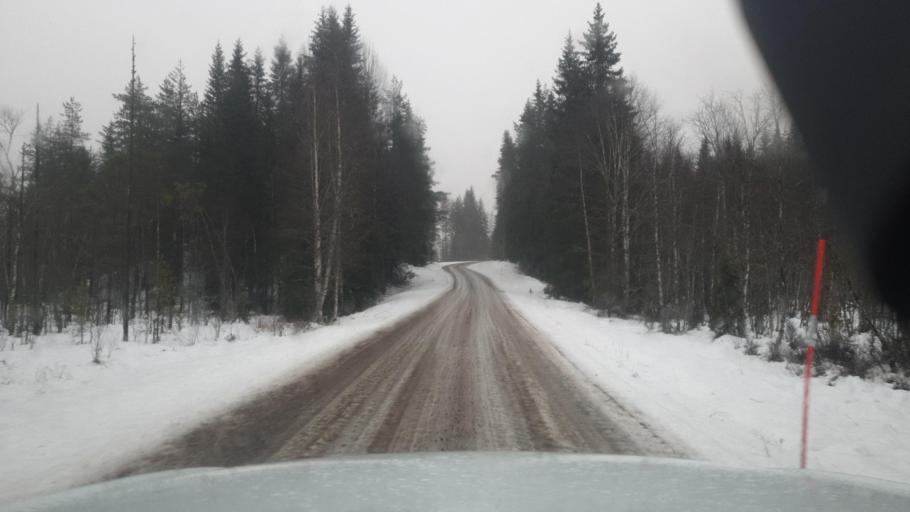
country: SE
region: Vaermland
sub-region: Eda Kommun
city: Charlottenberg
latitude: 60.0500
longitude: 12.5692
